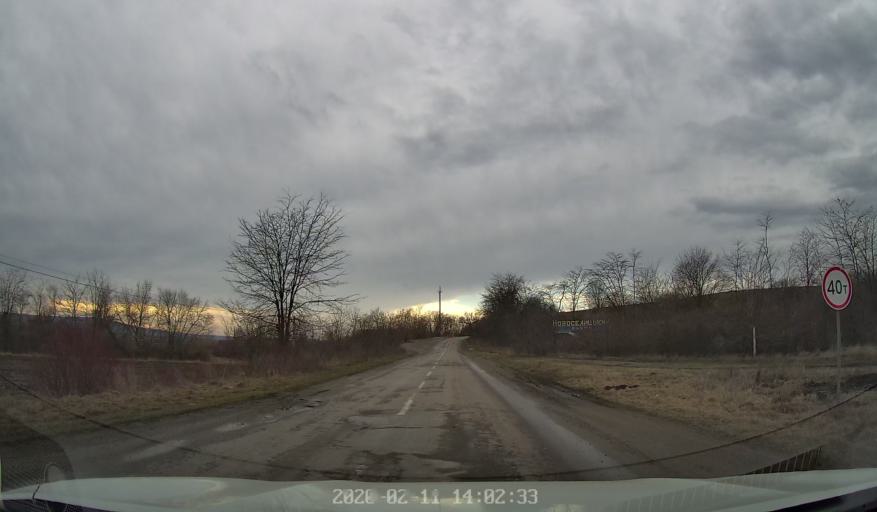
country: RO
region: Botosani
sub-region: Comuna Paltinis
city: Paltinis
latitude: 48.2616
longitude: 26.6118
